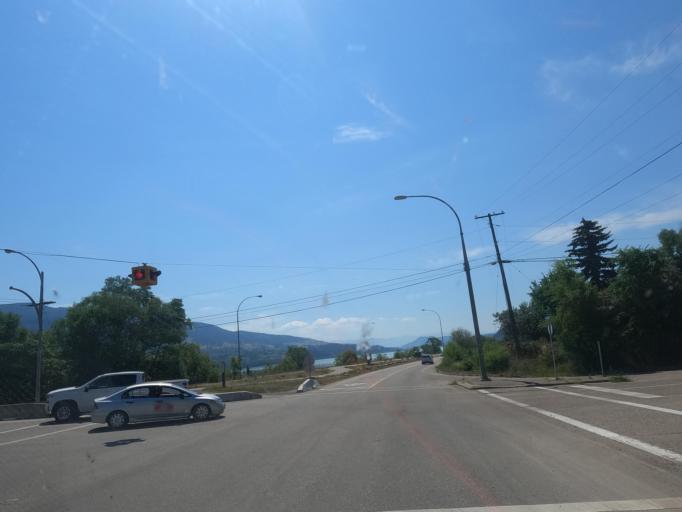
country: CA
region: British Columbia
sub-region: Regional District of North Okanagan
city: Vernon
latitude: 50.1107
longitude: -119.3876
